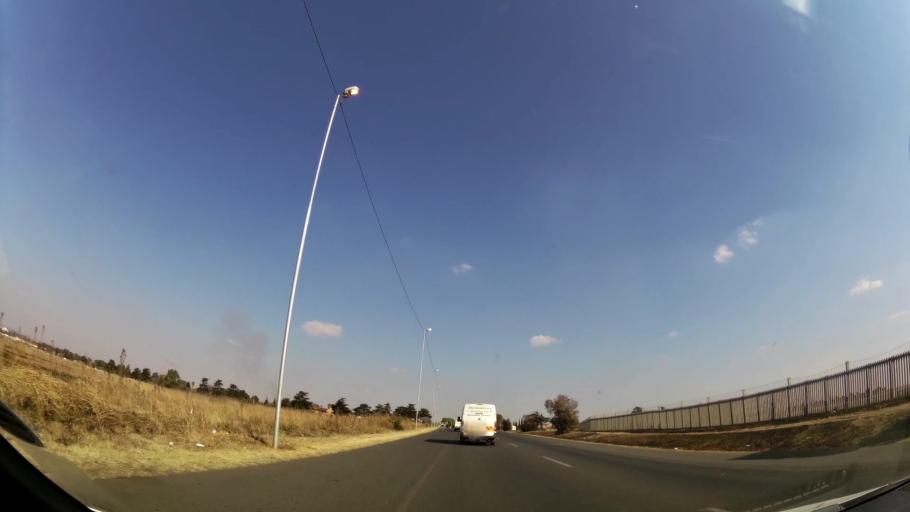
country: ZA
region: Gauteng
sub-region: Ekurhuleni Metropolitan Municipality
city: Boksburg
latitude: -26.2394
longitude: 28.2945
